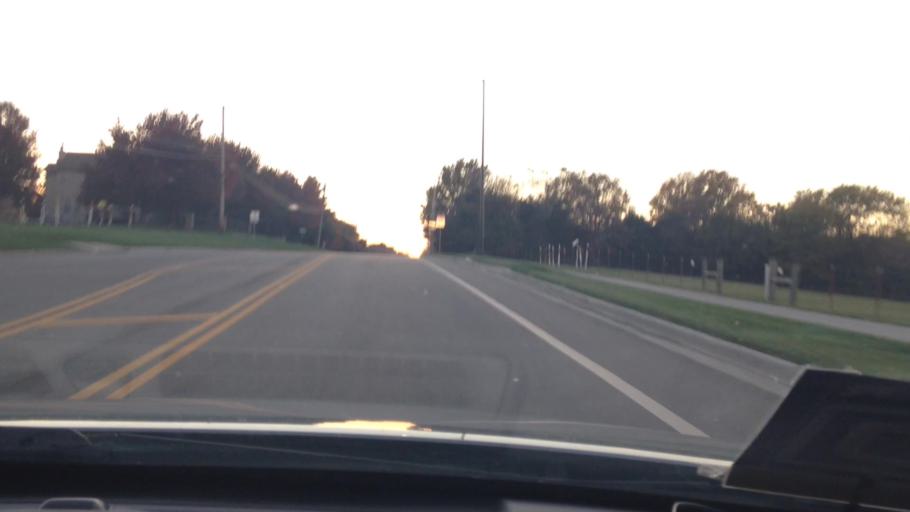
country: US
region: Kansas
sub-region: Johnson County
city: Olathe
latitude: 38.8692
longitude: -94.7432
